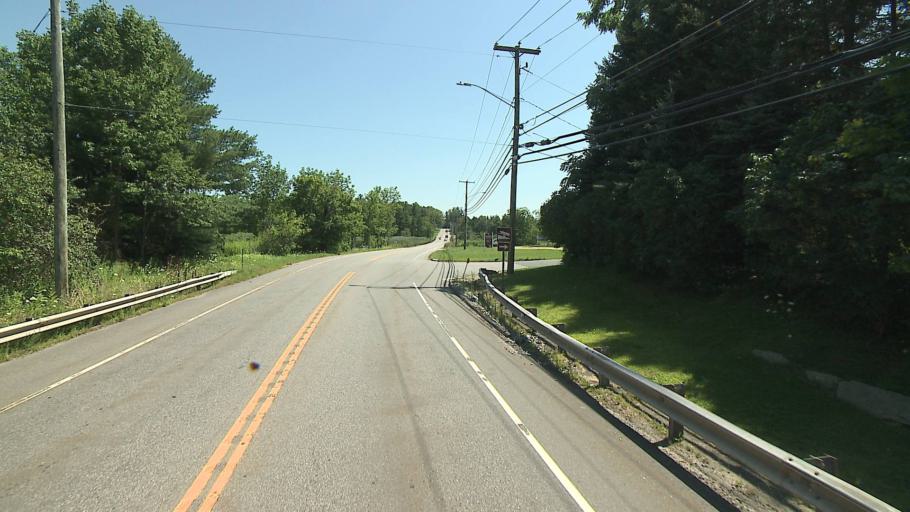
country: US
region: Connecticut
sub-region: Litchfield County
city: West Torrington
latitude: 41.8311
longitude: -73.2388
